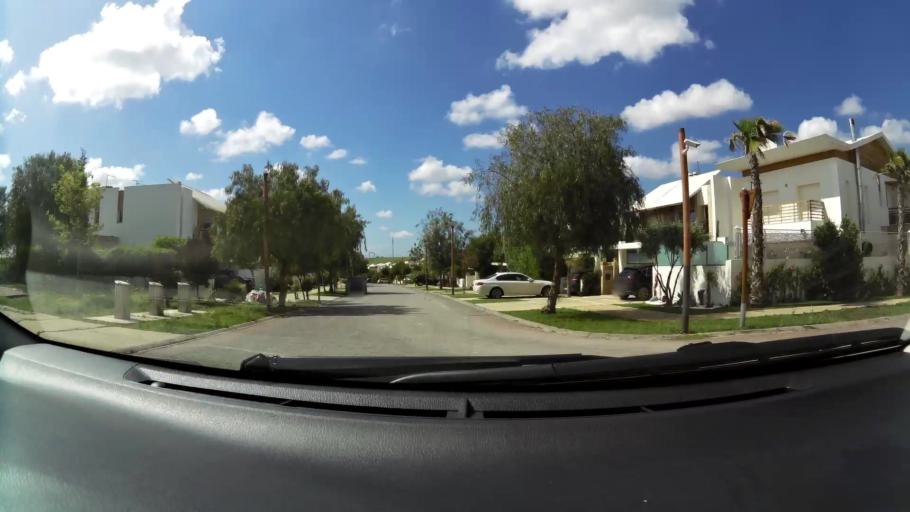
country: MA
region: Grand Casablanca
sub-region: Mediouna
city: Mediouna
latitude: 33.4899
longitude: -7.5838
